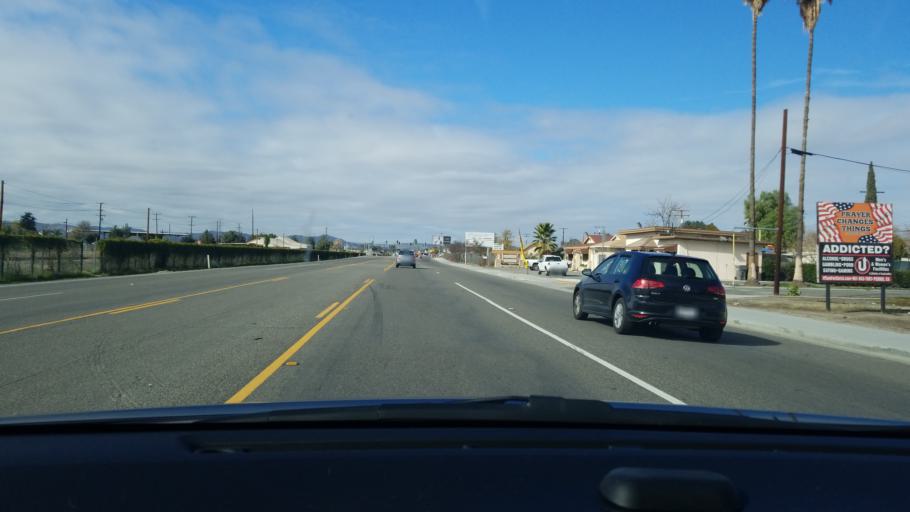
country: US
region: California
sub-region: Riverside County
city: Romoland
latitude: 33.7468
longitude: -117.1769
